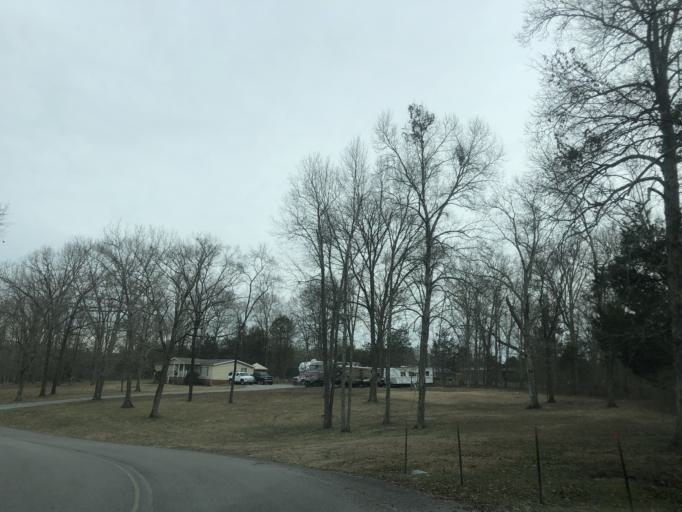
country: US
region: Tennessee
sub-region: Wilson County
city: Lebanon
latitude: 36.2537
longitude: -86.2675
